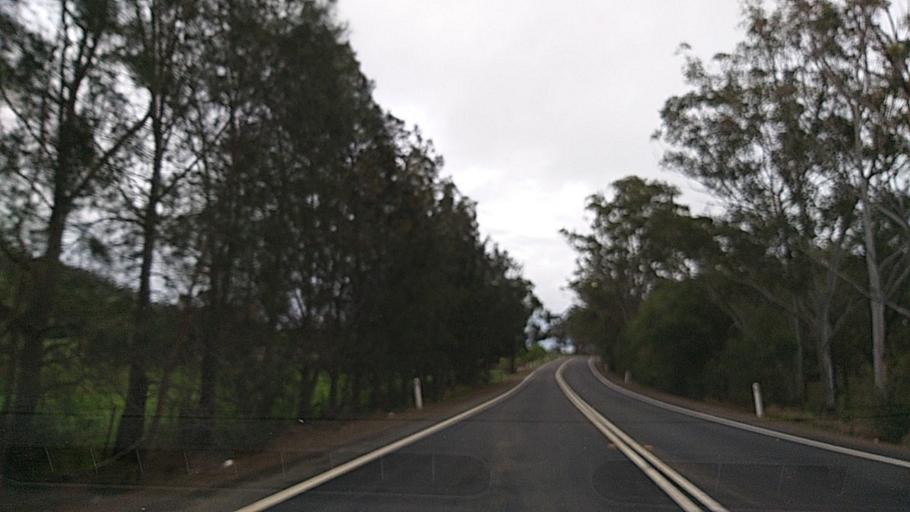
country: AU
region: New South Wales
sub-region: Camden
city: Camden South
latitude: -34.1267
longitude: 150.7012
